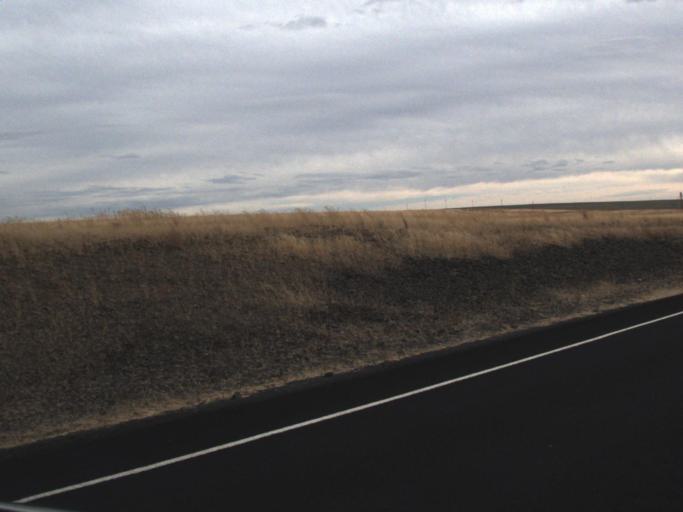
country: US
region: Washington
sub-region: Okanogan County
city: Coulee Dam
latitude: 47.7777
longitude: -118.7298
